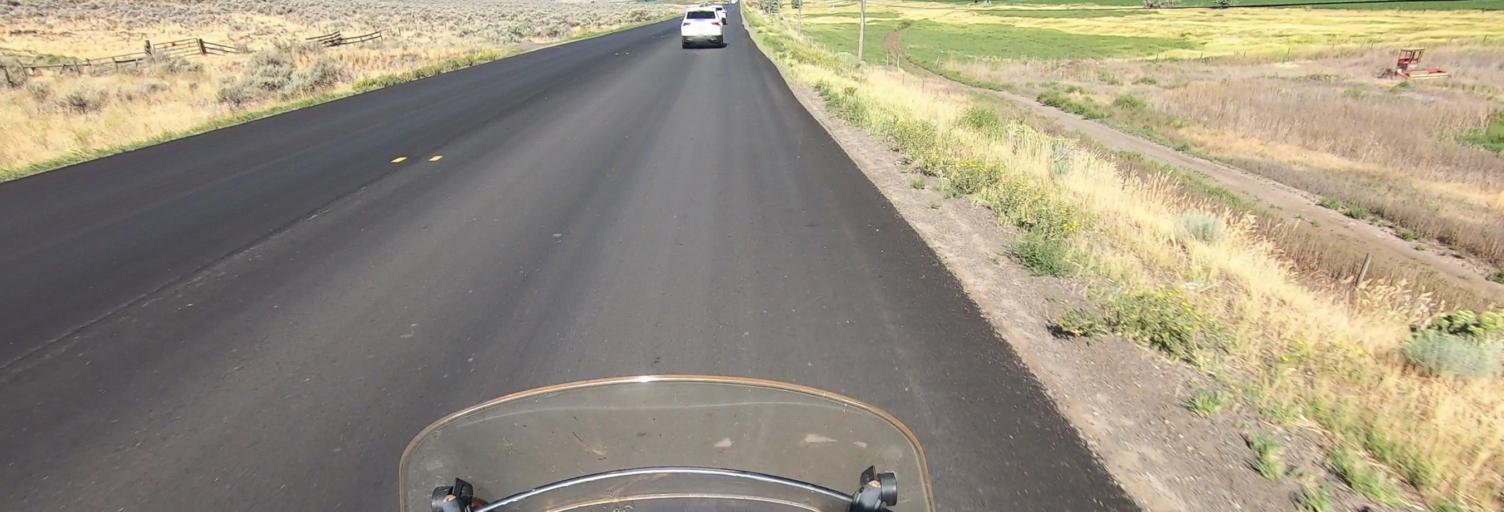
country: CA
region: British Columbia
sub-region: Thompson-Nicola Regional District
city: Ashcroft
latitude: 50.7907
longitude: -121.2370
